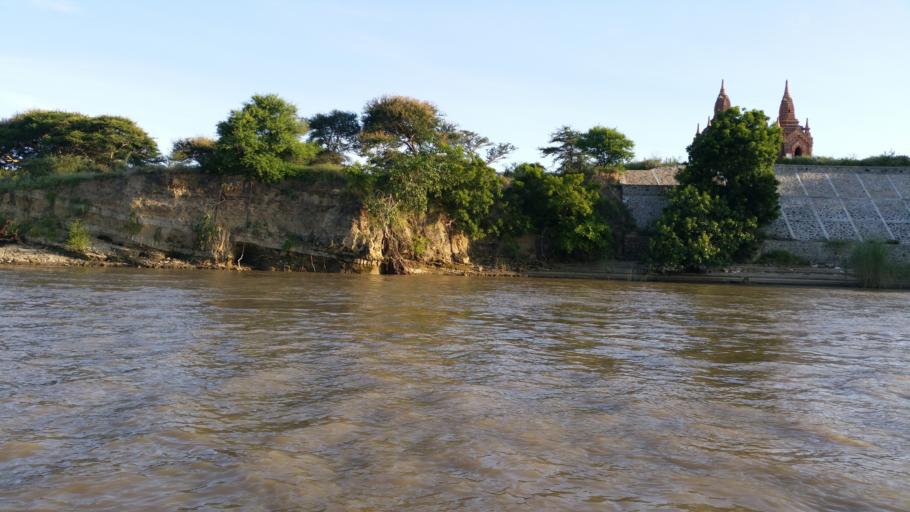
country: MM
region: Magway
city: Pakokku
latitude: 21.1845
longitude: 94.8720
